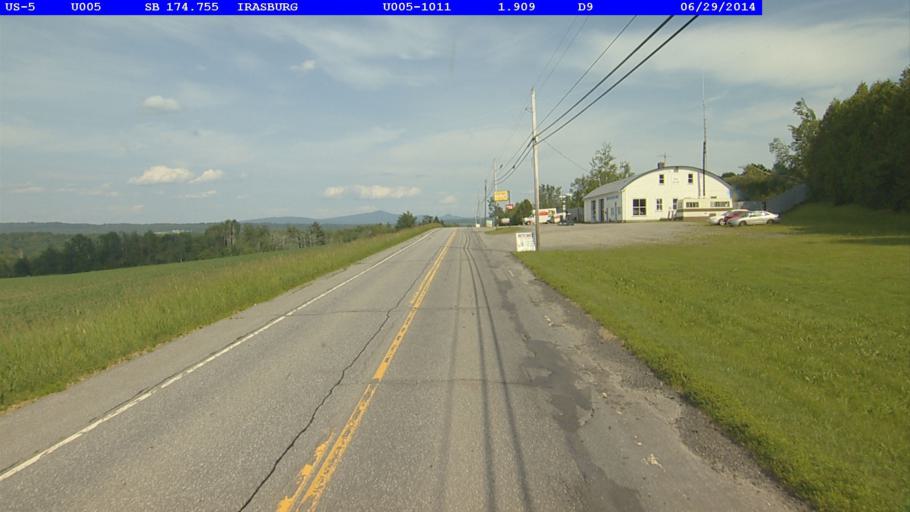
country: US
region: Vermont
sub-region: Orleans County
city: Newport
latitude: 44.8264
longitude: -72.2388
